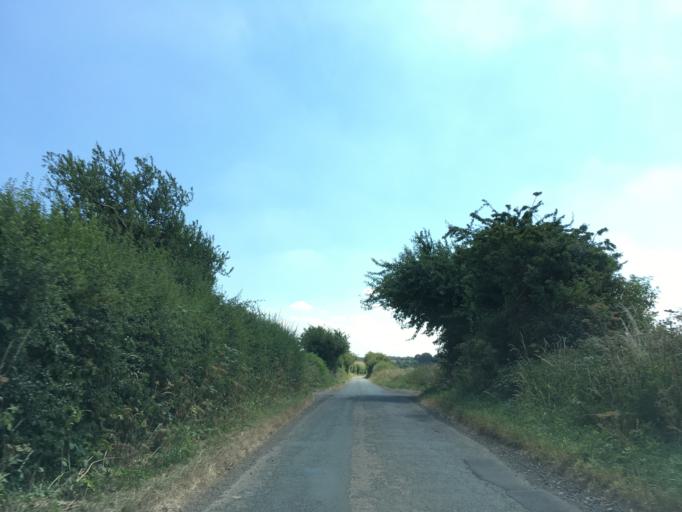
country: GB
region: England
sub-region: Gloucestershire
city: Chalford
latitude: 51.7084
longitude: -2.1119
